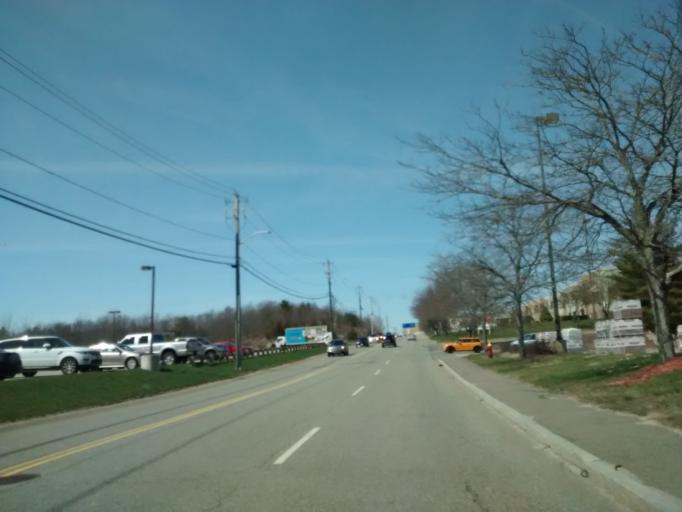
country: US
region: Massachusetts
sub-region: Norfolk County
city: Avon
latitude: 42.1309
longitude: -71.0669
